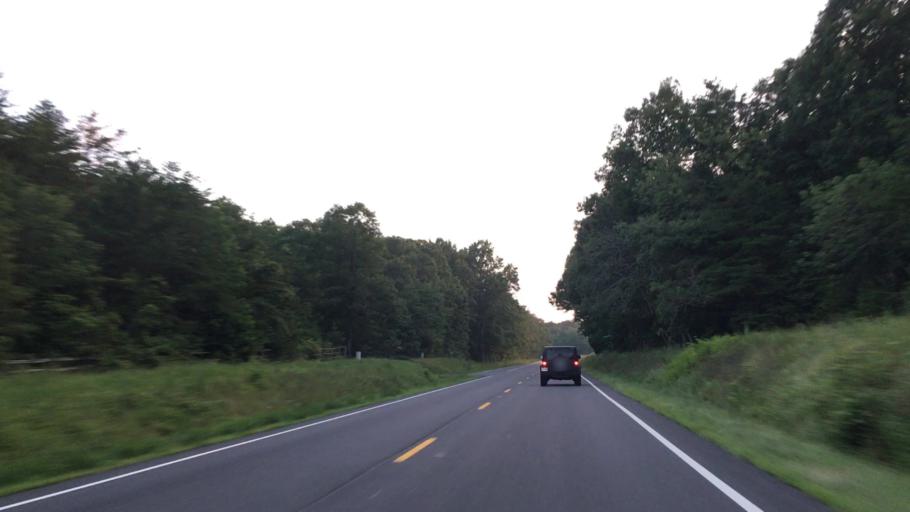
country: US
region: Virginia
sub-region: Culpeper County
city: Culpeper
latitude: 38.2905
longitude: -77.8589
